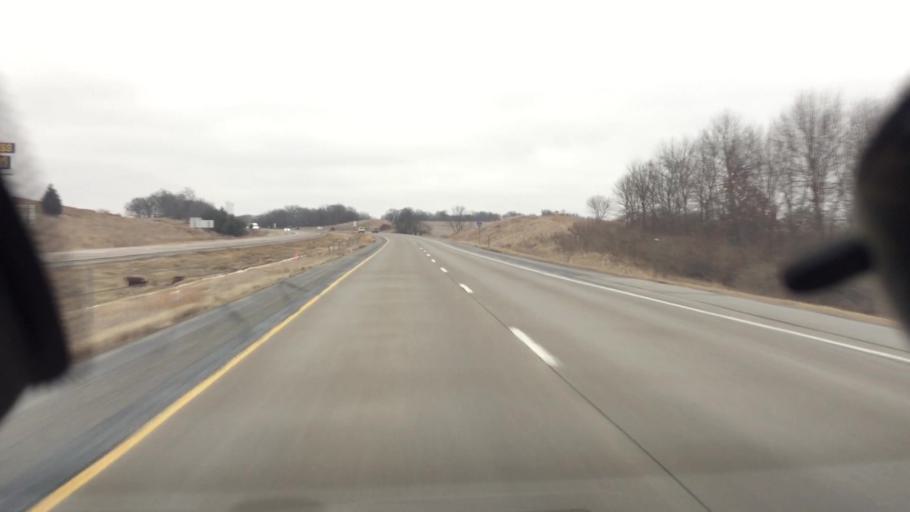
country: US
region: Iowa
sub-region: Cedar County
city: West Branch
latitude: 41.6756
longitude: -91.4373
